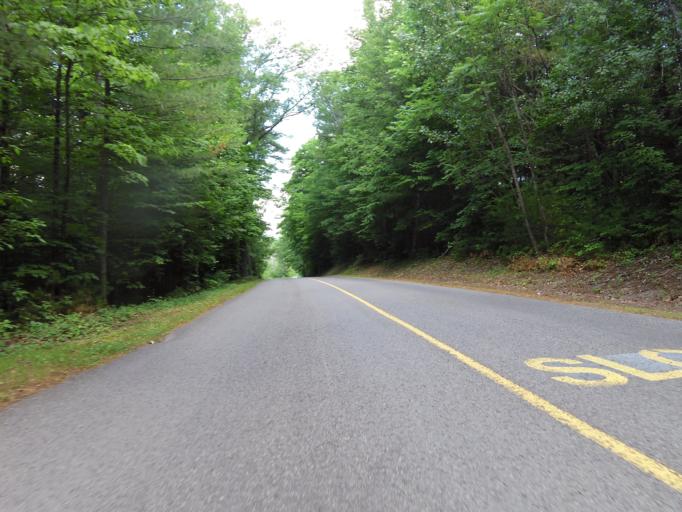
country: CA
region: Ontario
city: Arnprior
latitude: 45.4836
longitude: -76.2166
